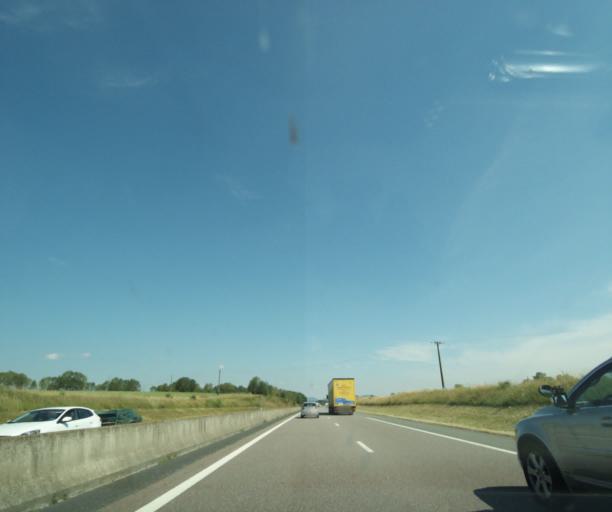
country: FR
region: Lorraine
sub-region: Departement de Meurthe-et-Moselle
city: Colombey-les-Belles
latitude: 48.5540
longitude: 5.8923
